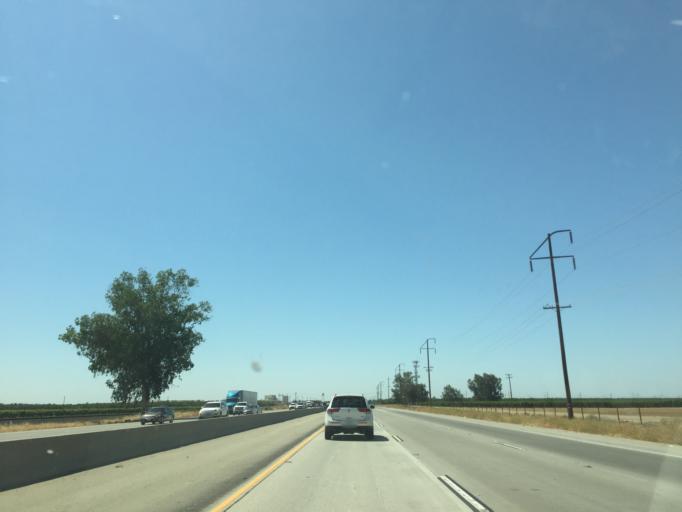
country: US
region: California
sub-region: Kern County
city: Rosedale
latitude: 35.4870
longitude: -119.1475
